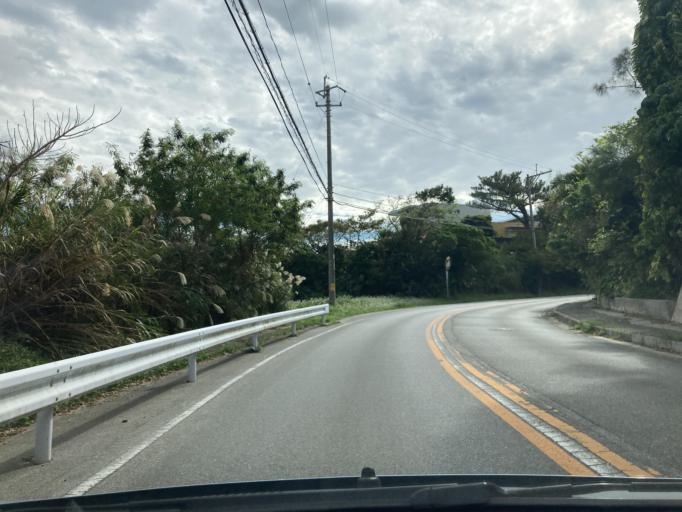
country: JP
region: Okinawa
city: Ishikawa
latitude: 26.4348
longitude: 127.7781
